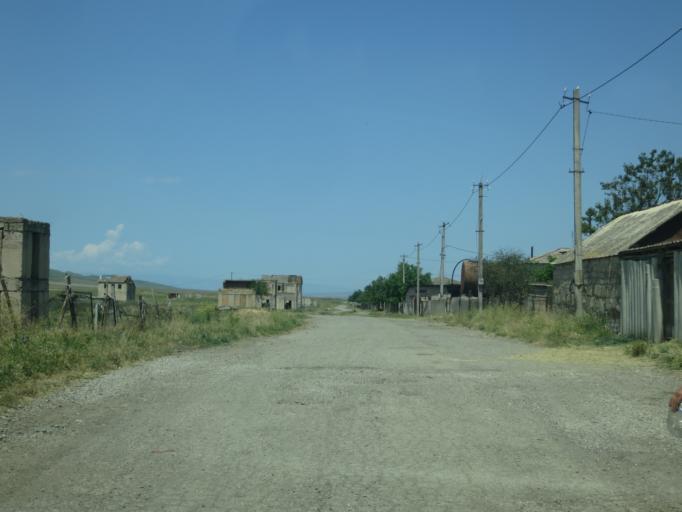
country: AZ
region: Agstafa
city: Saloglu
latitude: 41.5010
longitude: 45.3778
